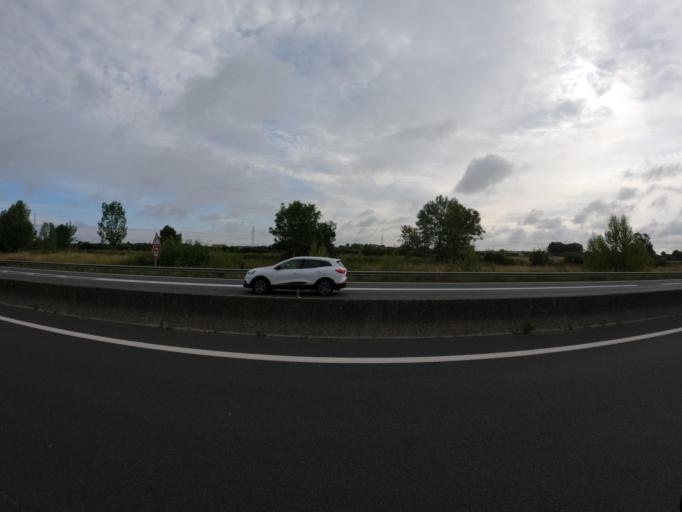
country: FR
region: Centre
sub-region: Departement d'Indre-et-Loire
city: Villandry
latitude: 47.3095
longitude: 0.5124
